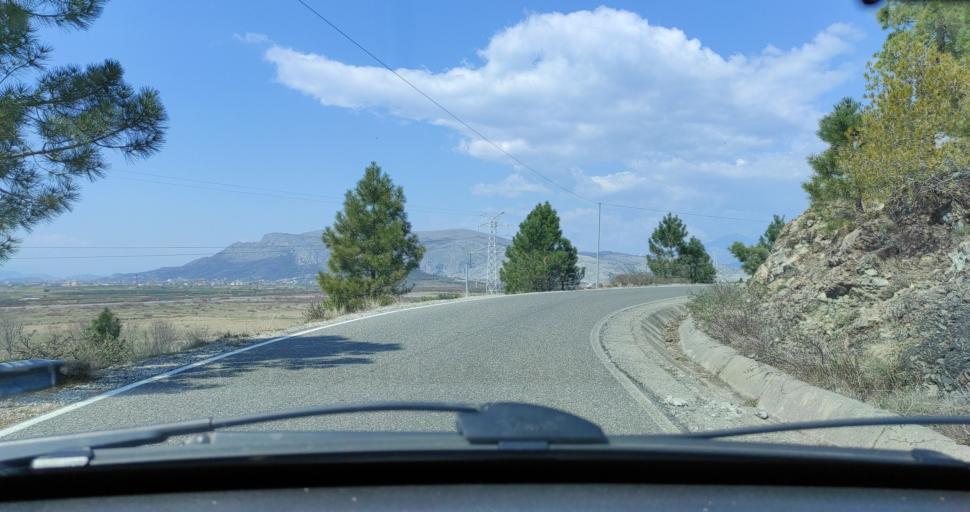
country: AL
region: Shkoder
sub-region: Rrethi i Shkodres
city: Hajmel
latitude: 41.9828
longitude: 19.6440
